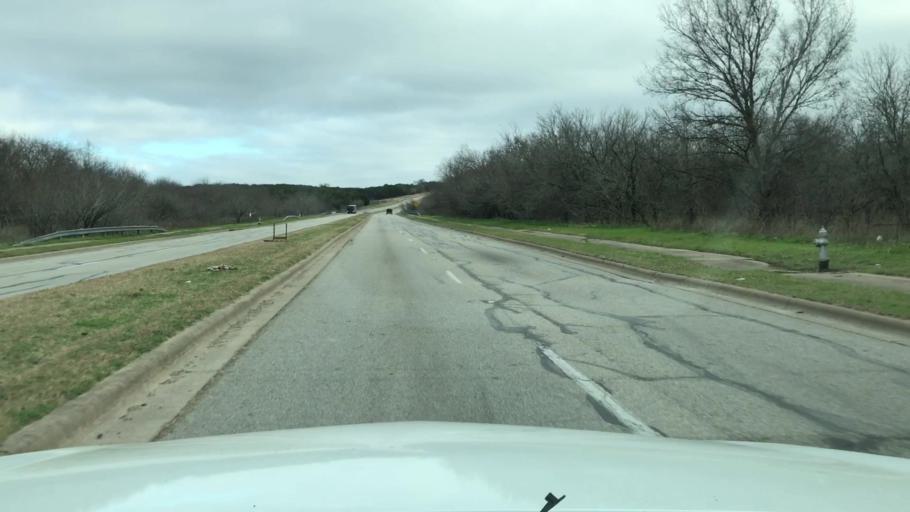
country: US
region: Texas
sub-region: Travis County
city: Austin
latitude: 30.1960
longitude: -97.7253
